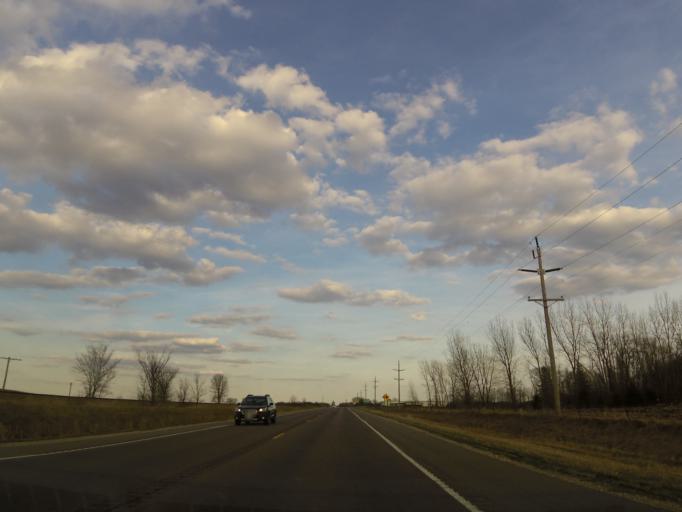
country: US
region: Minnesota
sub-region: Renville County
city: Hector
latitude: 44.7242
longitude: -94.5244
